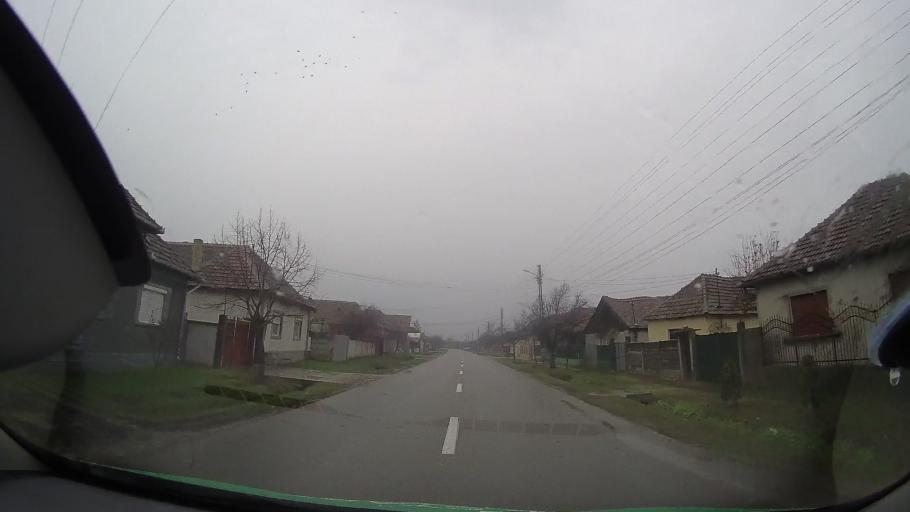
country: RO
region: Bihor
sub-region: Comuna Tulca
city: Tulca
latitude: 46.7928
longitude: 21.7667
